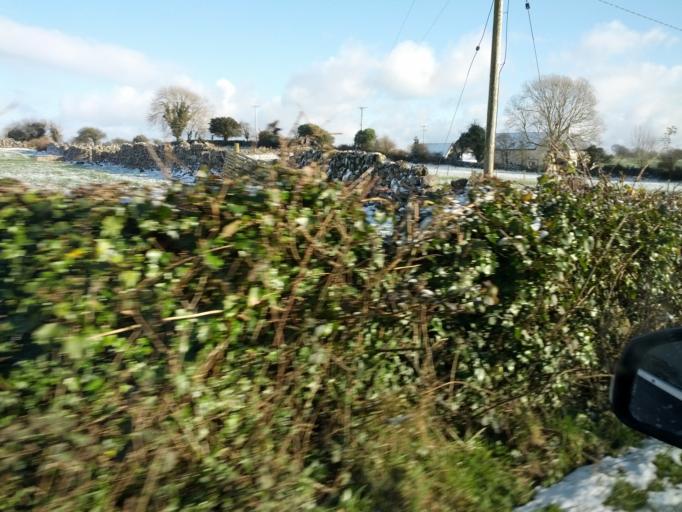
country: IE
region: Connaught
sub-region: County Galway
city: Athenry
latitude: 53.1851
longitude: -8.7862
